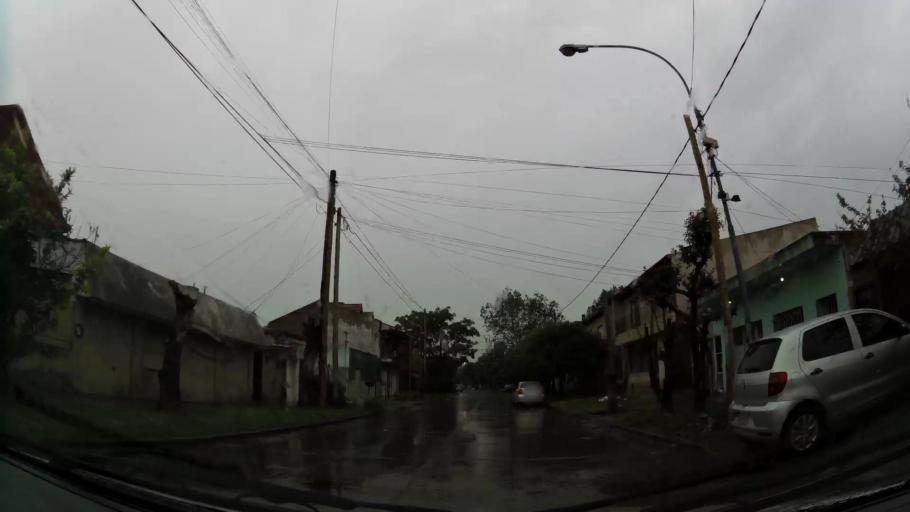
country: AR
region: Buenos Aires
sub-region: Partido de Lanus
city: Lanus
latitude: -34.7121
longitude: -58.4159
